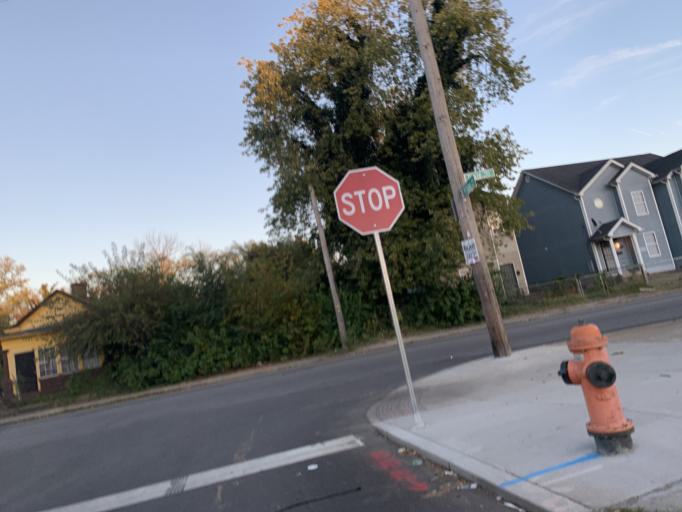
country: US
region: Kentucky
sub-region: Jefferson County
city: Louisville
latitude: 38.2347
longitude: -85.7881
